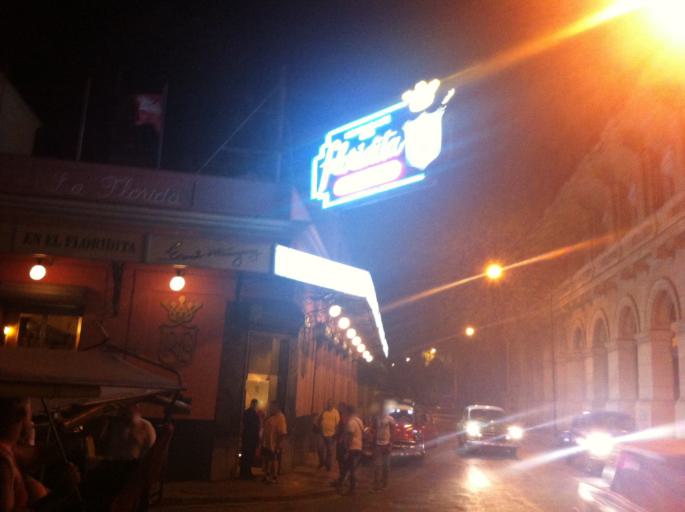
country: CU
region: La Habana
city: La Habana Vieja
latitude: 23.1406
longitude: -82.3534
